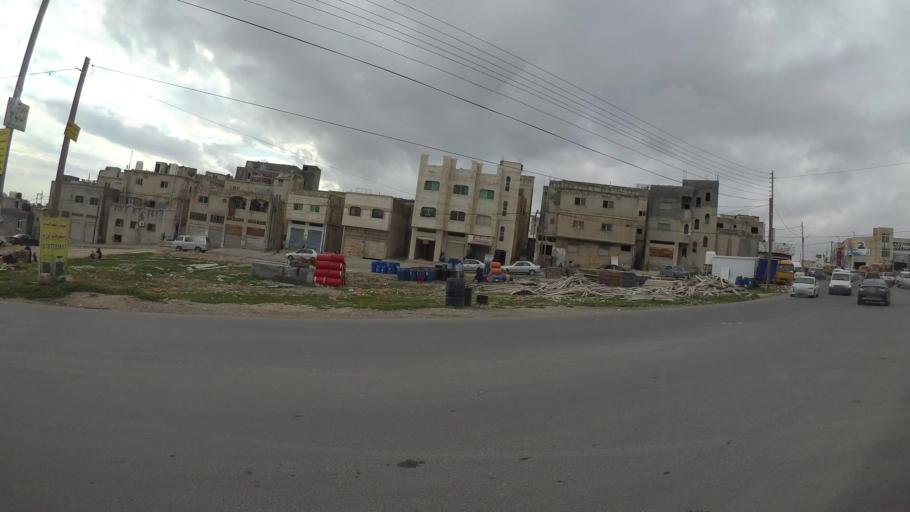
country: JO
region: Amman
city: Wadi as Sir
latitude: 31.9368
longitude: 35.8454
